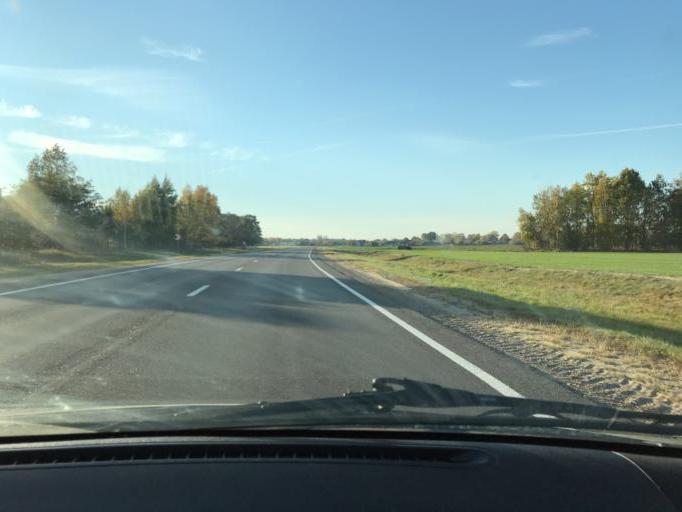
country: BY
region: Brest
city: Horad Kobryn
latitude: 52.2074
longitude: 24.5734
